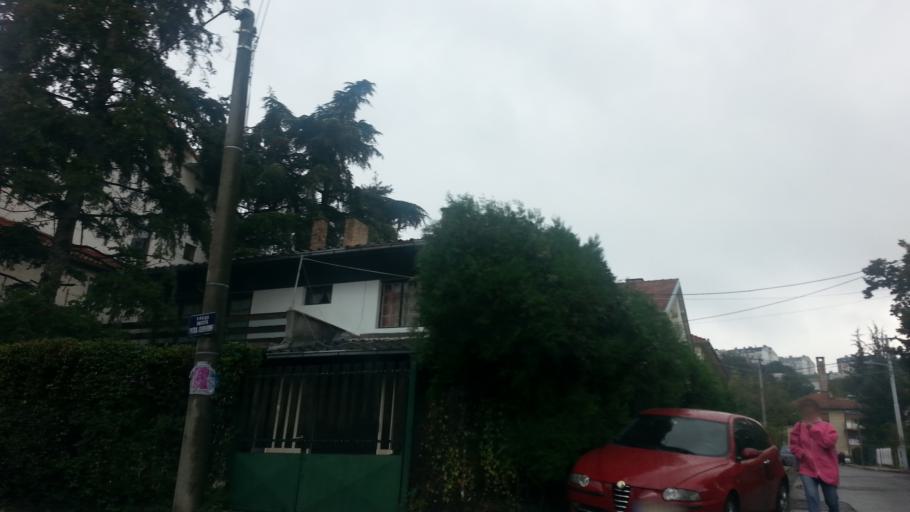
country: RS
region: Central Serbia
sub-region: Belgrade
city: Rakovica
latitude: 44.7468
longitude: 20.4388
